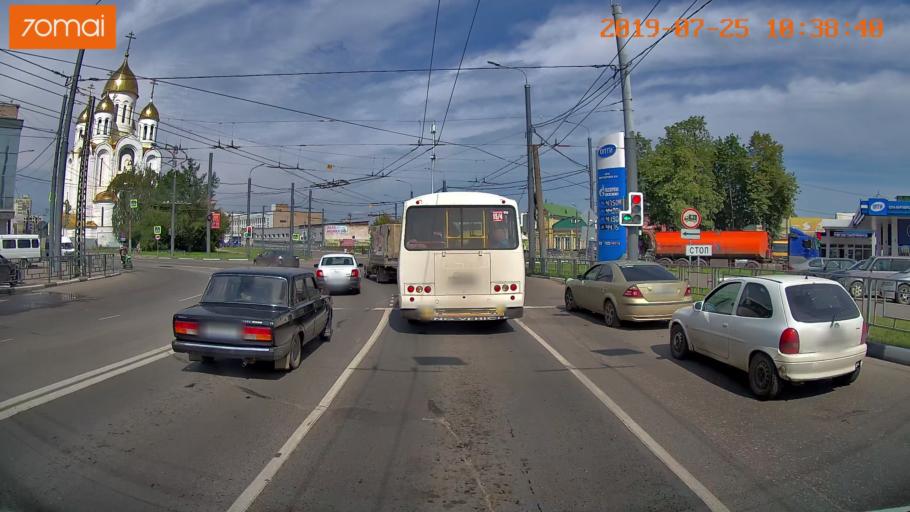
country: RU
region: Ivanovo
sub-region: Gorod Ivanovo
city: Ivanovo
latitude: 57.0159
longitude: 40.9842
